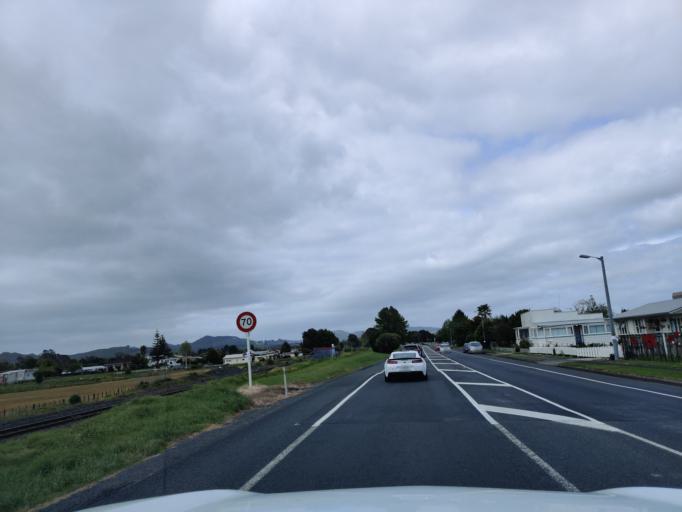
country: NZ
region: Waikato
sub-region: Waikato District
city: Ngaruawahia
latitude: -37.5345
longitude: 175.1592
